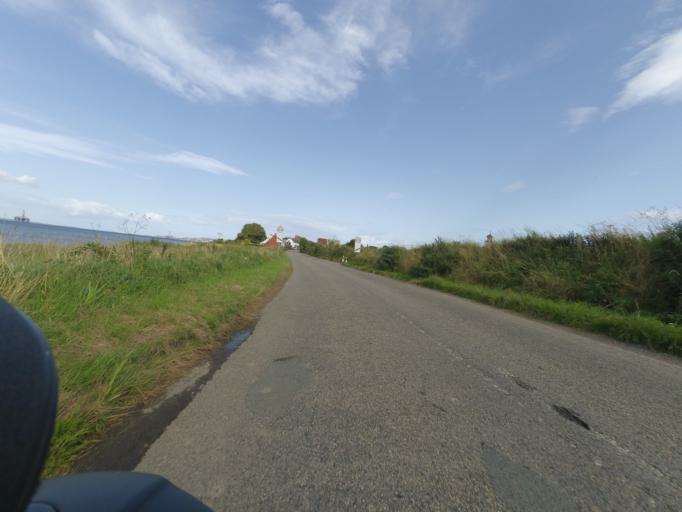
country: GB
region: Scotland
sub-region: Highland
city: Invergordon
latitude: 57.6574
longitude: -4.1541
